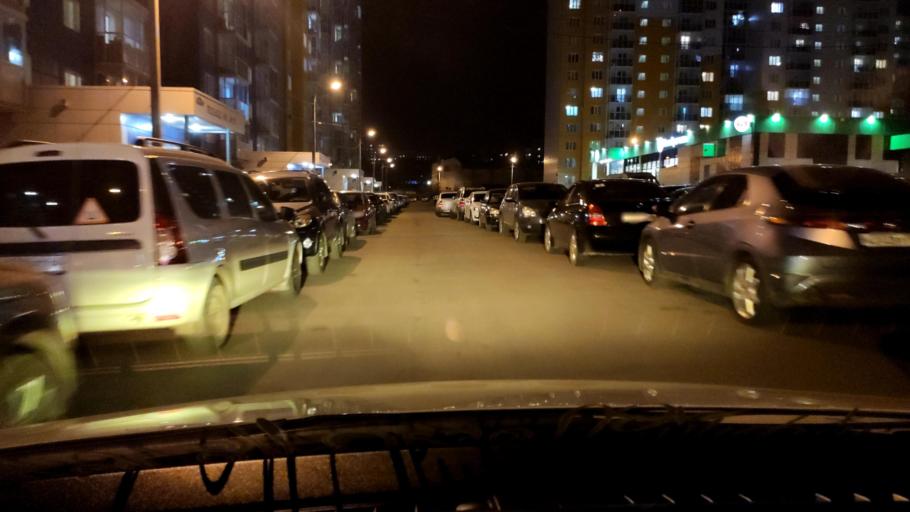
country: RU
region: Voronezj
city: Podgornoye
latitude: 51.6869
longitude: 39.1351
